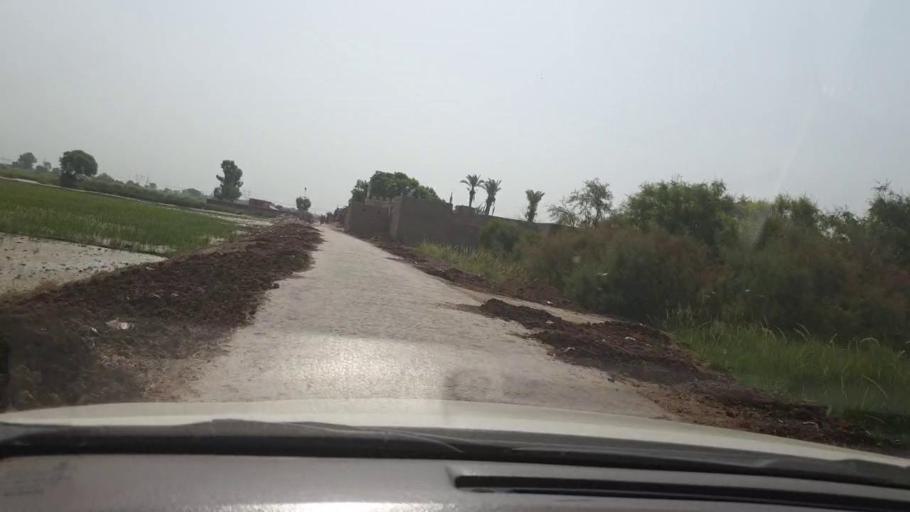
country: PK
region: Sindh
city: Rustam jo Goth
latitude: 27.9770
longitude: 68.8003
